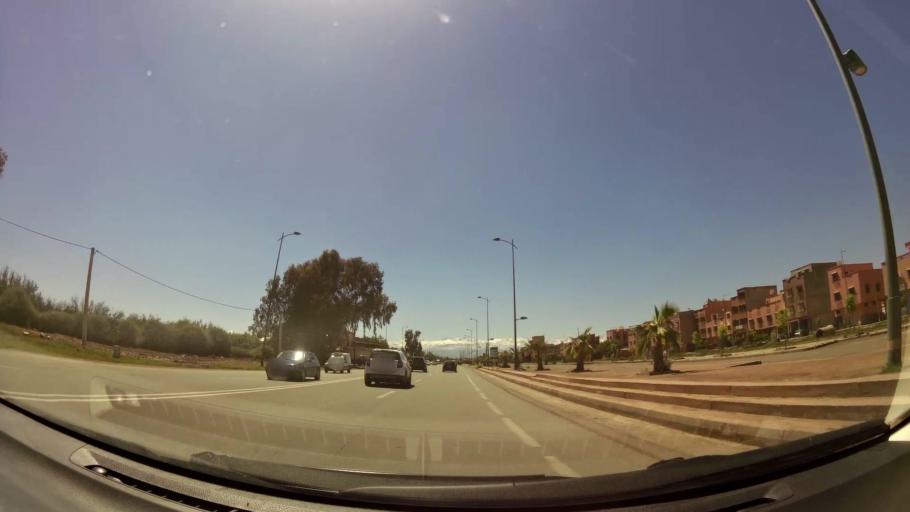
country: MA
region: Marrakech-Tensift-Al Haouz
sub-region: Marrakech
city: Marrakesh
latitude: 31.5657
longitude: -7.9800
